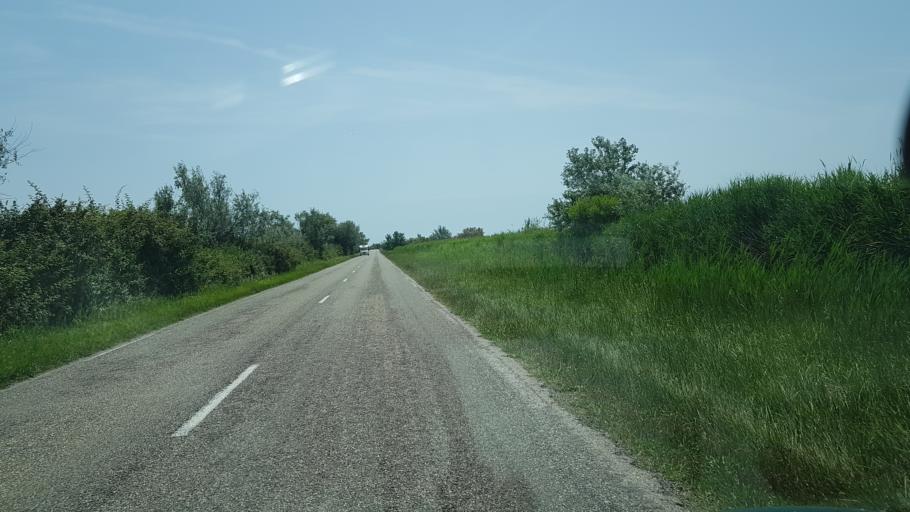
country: FR
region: Languedoc-Roussillon
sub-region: Departement du Gard
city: Saint-Gilles
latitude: 43.5762
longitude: 4.5216
